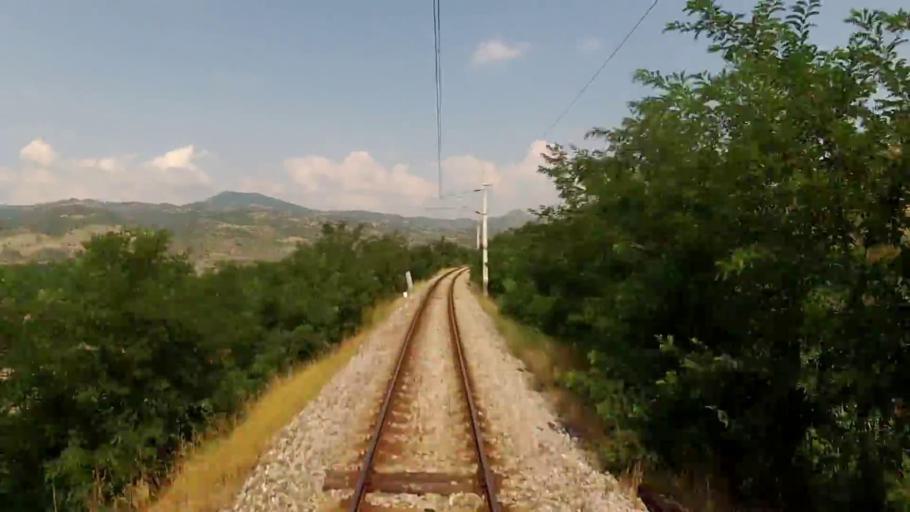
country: BG
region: Blagoevgrad
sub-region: Obshtina Sandanski
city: Sandanski
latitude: 41.5663
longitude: 23.2424
